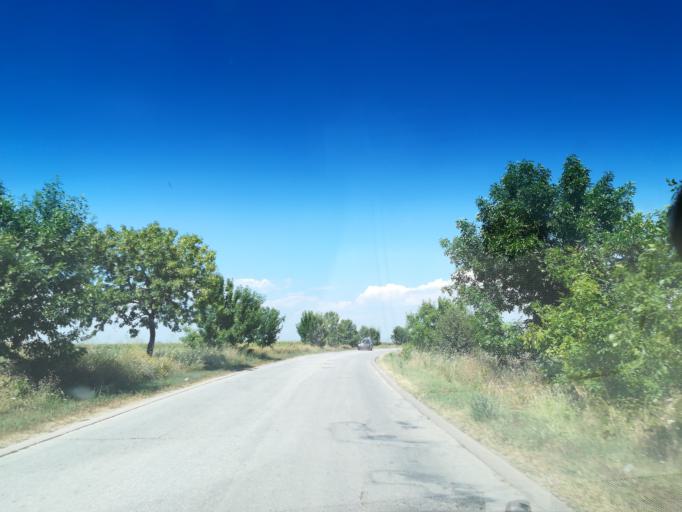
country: BG
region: Plovdiv
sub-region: Obshtina Sadovo
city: Sadovo
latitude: 42.0370
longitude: 25.1243
